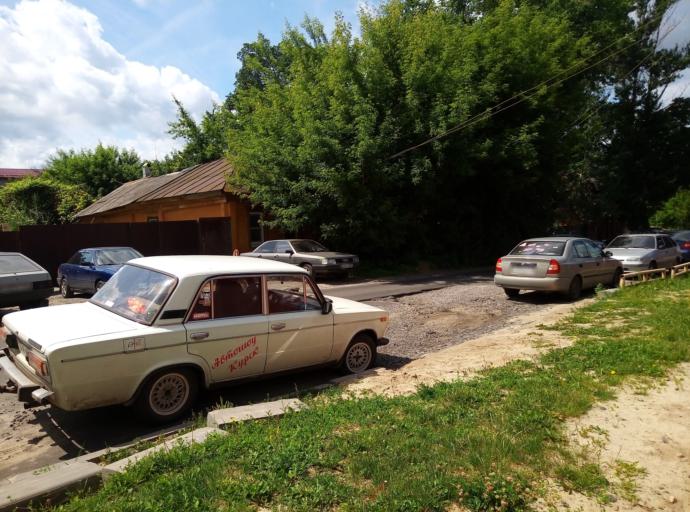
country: RU
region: Kursk
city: Kursk
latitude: 51.7360
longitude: 36.1890
